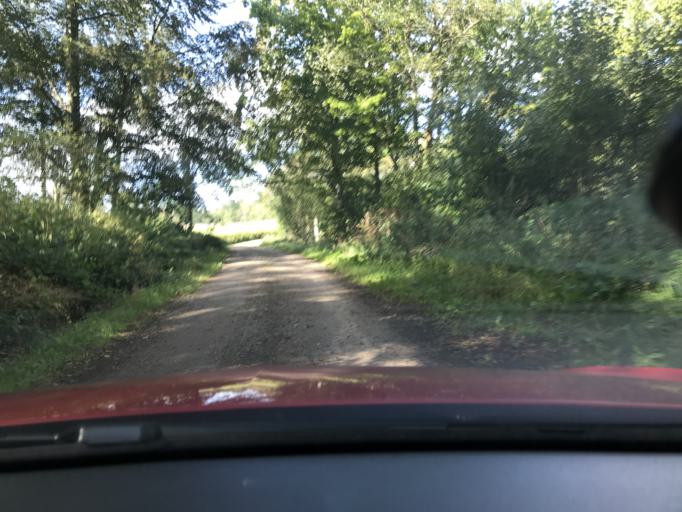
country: SE
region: Skane
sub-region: Hassleholms Kommun
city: Sosdala
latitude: 55.9996
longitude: 13.7050
